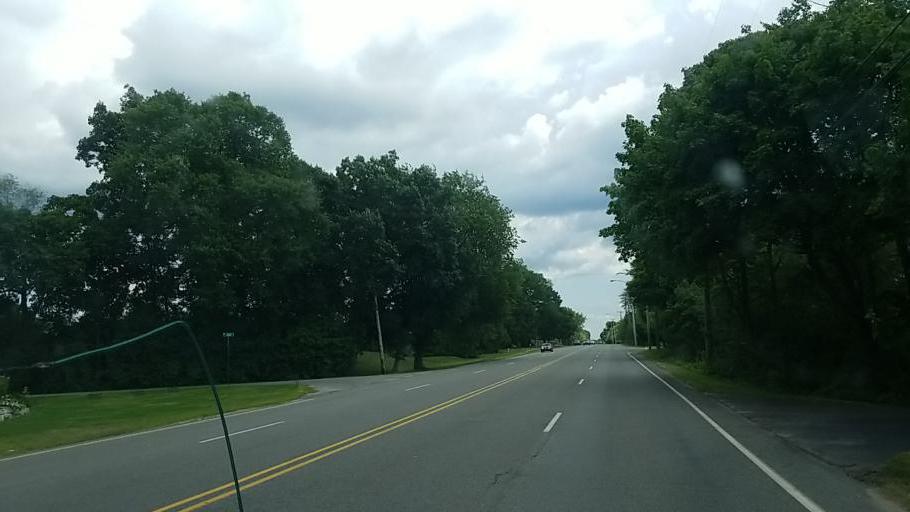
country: US
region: Michigan
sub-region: Kent County
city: East Grand Rapids
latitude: 42.9537
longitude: -85.5814
